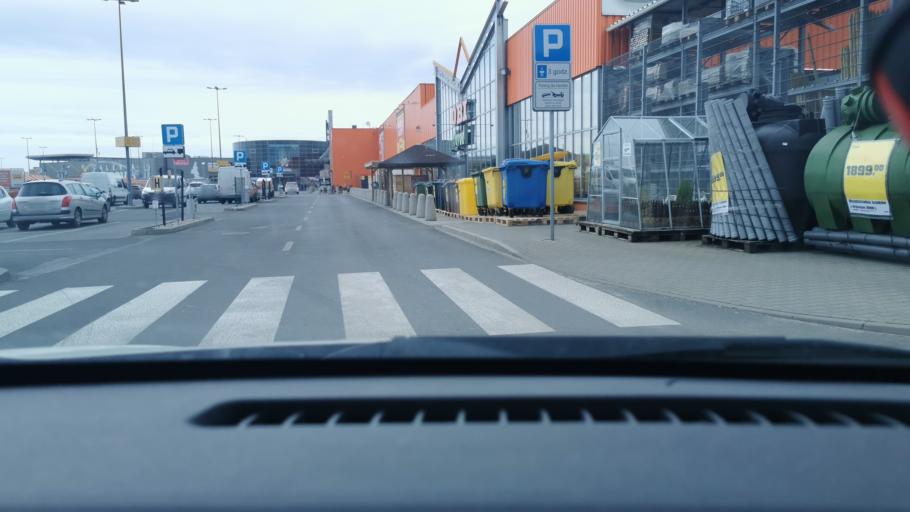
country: PL
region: Greater Poland Voivodeship
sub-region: Powiat ostrowski
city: Ostrow Wielkopolski
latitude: 51.6557
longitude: 17.8462
